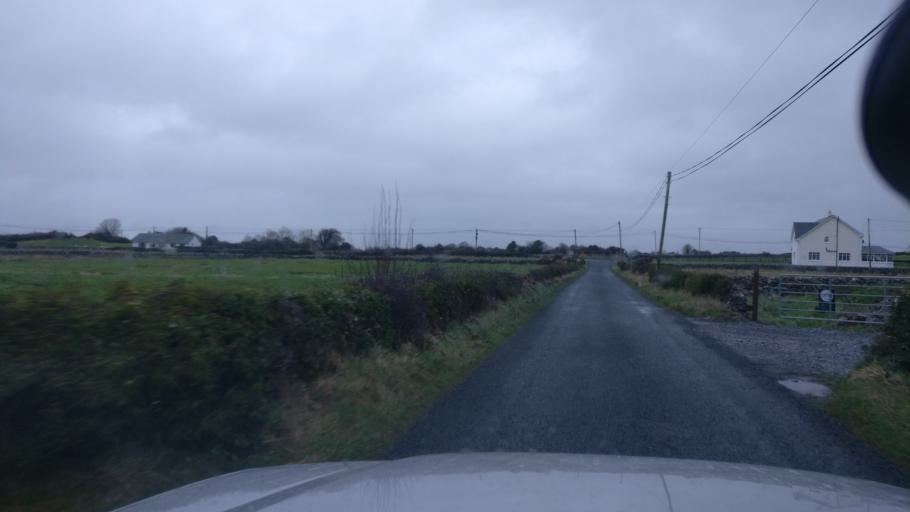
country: IE
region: Connaught
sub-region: County Galway
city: Loughrea
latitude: 53.2174
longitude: -8.6223
